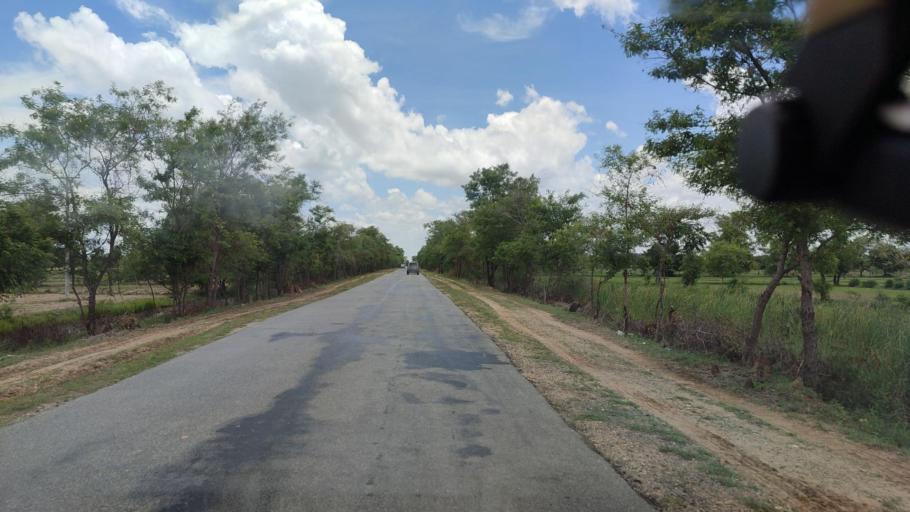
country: MM
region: Magway
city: Taungdwingyi
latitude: 20.1961
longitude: 95.3901
